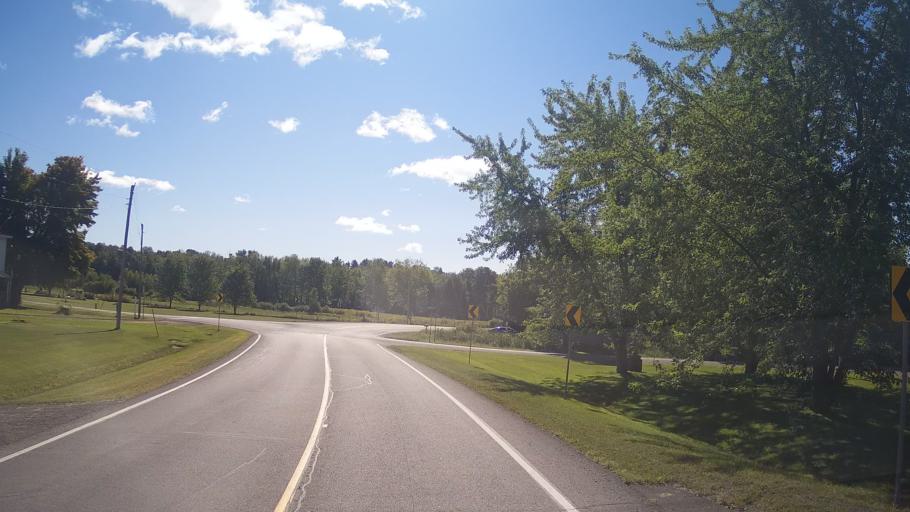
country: CA
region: Ontario
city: Prescott
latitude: 44.9021
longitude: -75.3990
